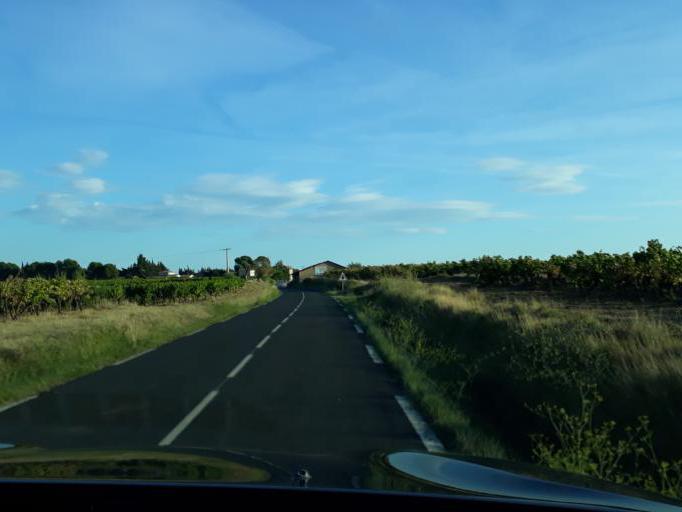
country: FR
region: Languedoc-Roussillon
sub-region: Departement de l'Herault
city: Pomerols
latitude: 43.4048
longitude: 3.4909
